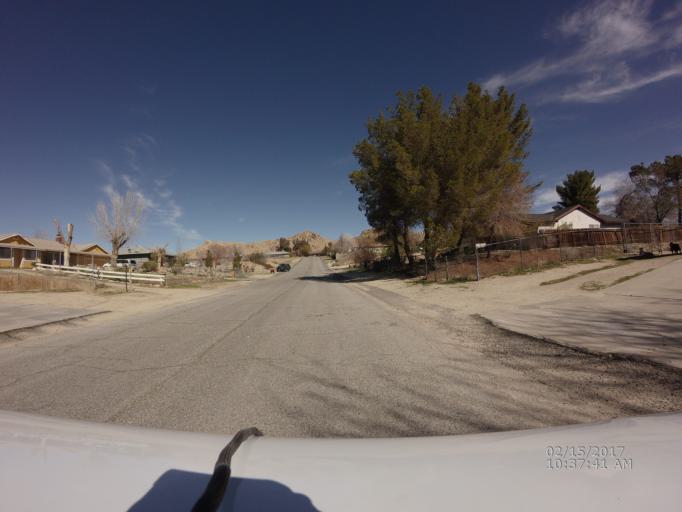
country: US
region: California
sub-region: Los Angeles County
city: Lake Los Angeles
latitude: 34.5841
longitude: -117.8549
